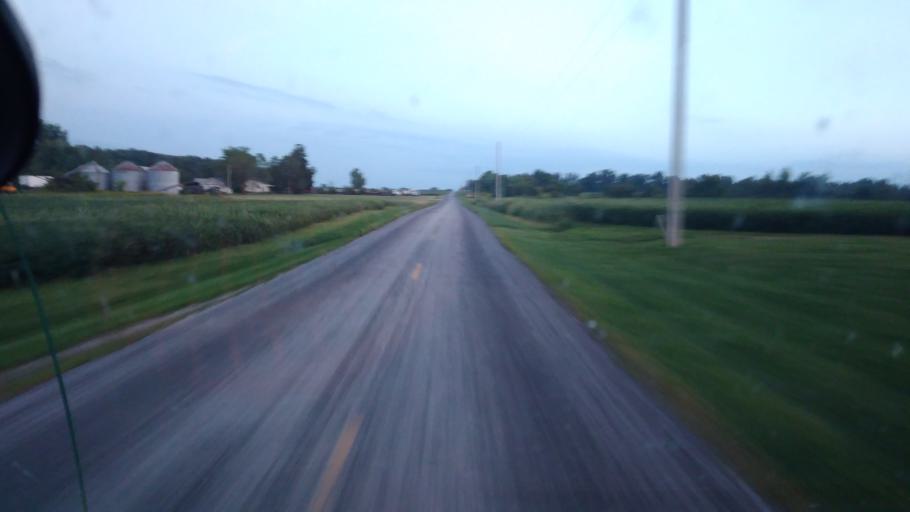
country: US
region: Ohio
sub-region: Hardin County
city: Kenton
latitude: 40.6388
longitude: -83.4578
